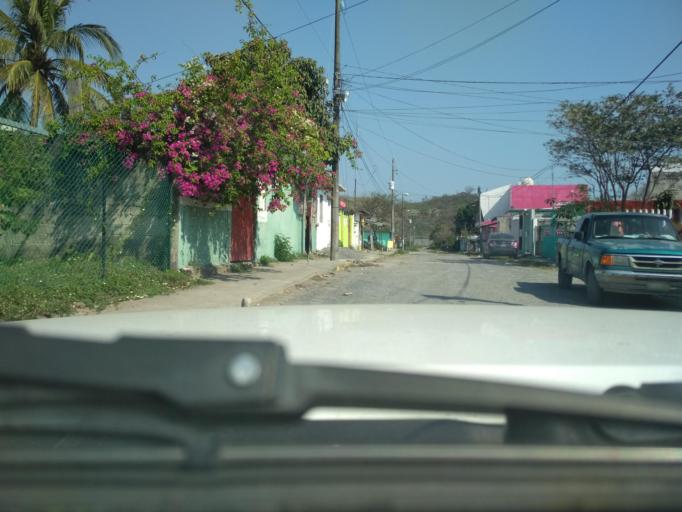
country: MX
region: Veracruz
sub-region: Veracruz
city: Colonia el Renacimiento
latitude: 19.2189
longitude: -96.2138
